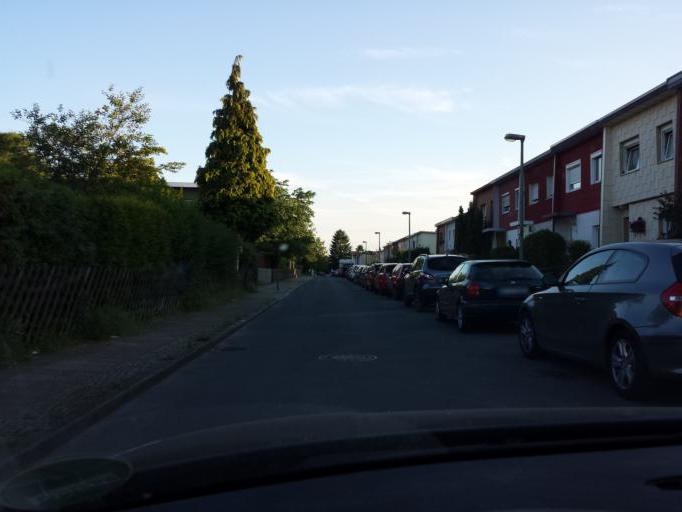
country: DE
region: Berlin
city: Lichtenrade
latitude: 52.4257
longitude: 13.4061
